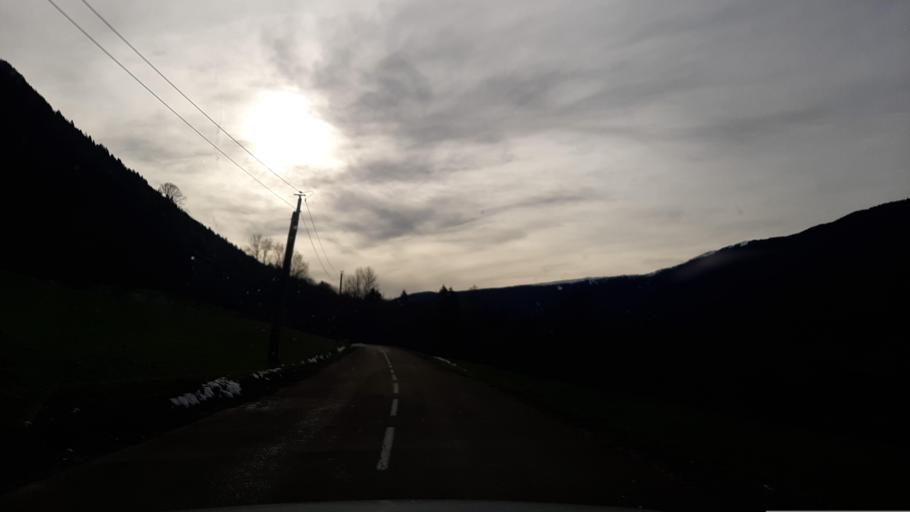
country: FR
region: Rhone-Alpes
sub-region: Departement de la Haute-Savoie
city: Cusy
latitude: 45.6781
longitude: 6.1126
